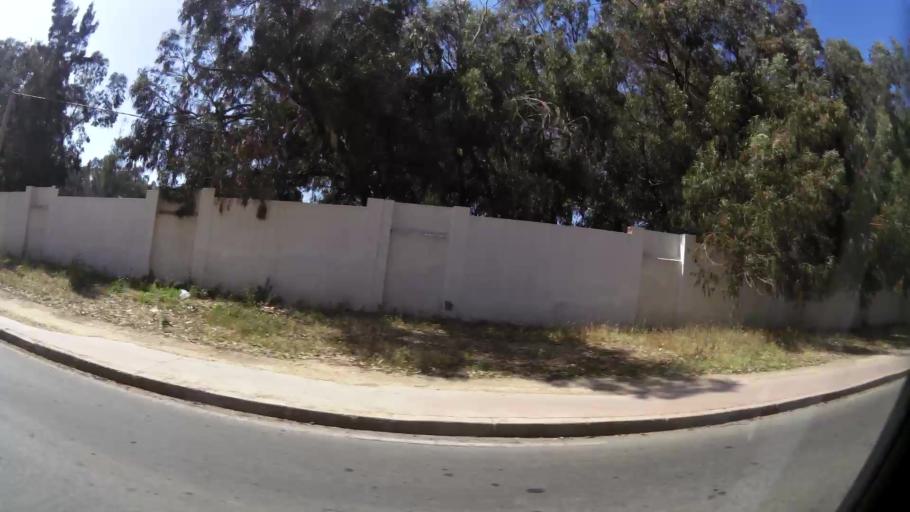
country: MA
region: Souss-Massa-Draa
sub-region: Inezgane-Ait Mellou
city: Inezgane
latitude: 30.3697
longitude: -9.5594
